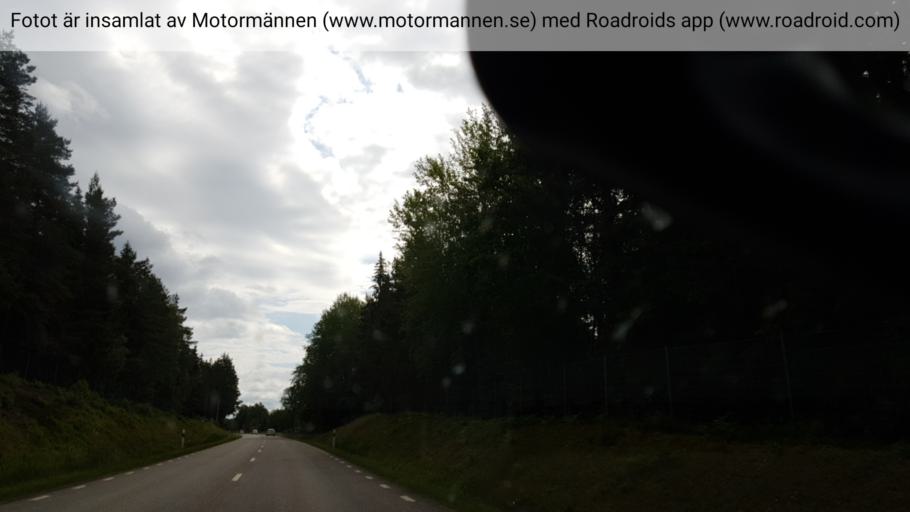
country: SE
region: Vaestra Goetaland
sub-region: Vara Kommun
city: Kvanum
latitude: 58.2148
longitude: 13.2176
